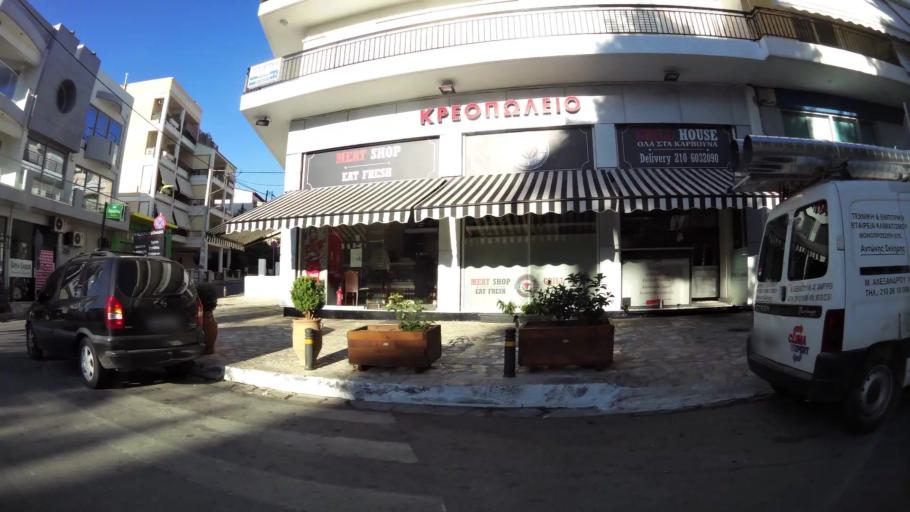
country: GR
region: Attica
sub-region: Nomarchia Anatolikis Attikis
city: Pallini
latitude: 38.0053
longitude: 23.8810
